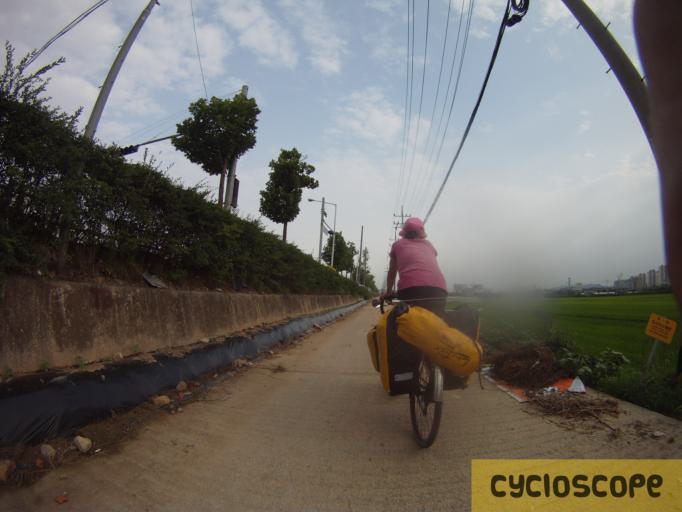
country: KR
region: Gyeonggi-do
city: Suwon-si
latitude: 37.2673
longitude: 126.9715
